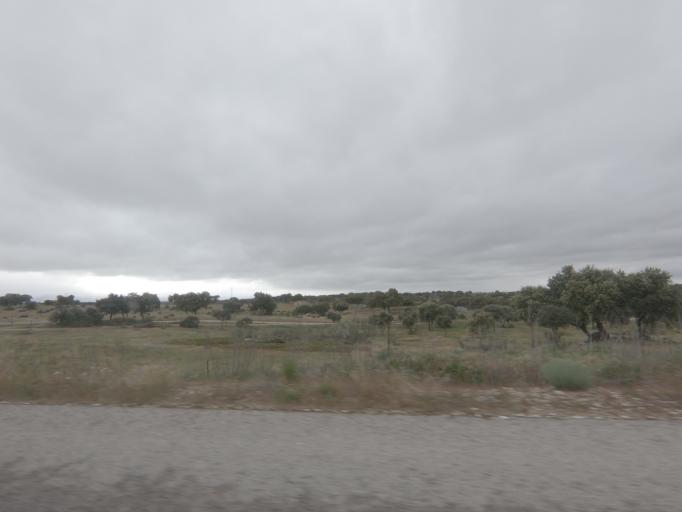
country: ES
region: Extremadura
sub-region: Provincia de Caceres
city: Caceres
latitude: 39.4052
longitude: -6.4204
